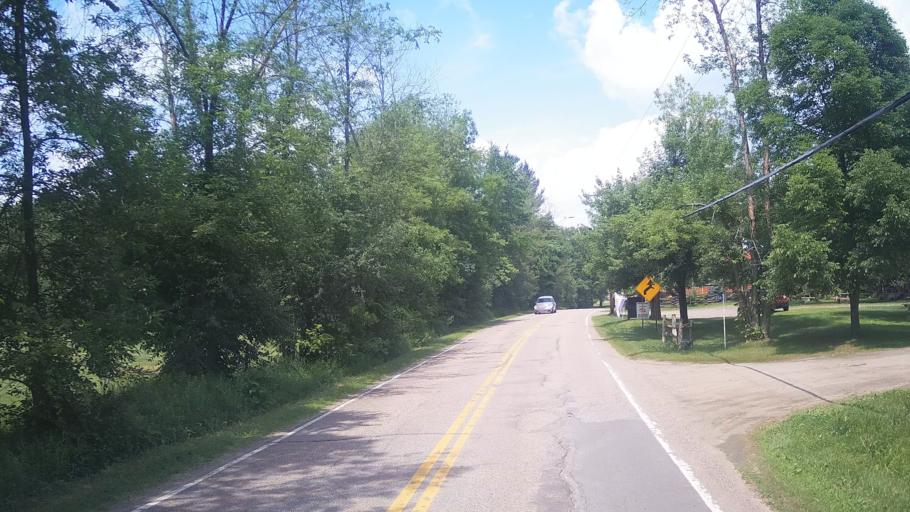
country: CA
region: Quebec
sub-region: Outaouais
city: Shawville
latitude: 45.5279
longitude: -76.4553
